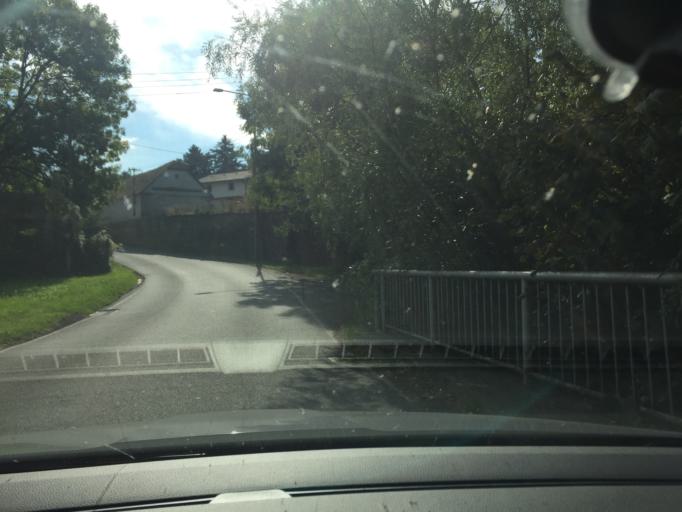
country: CZ
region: Central Bohemia
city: Cervene Pecky
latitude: 49.9744
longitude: 15.2345
